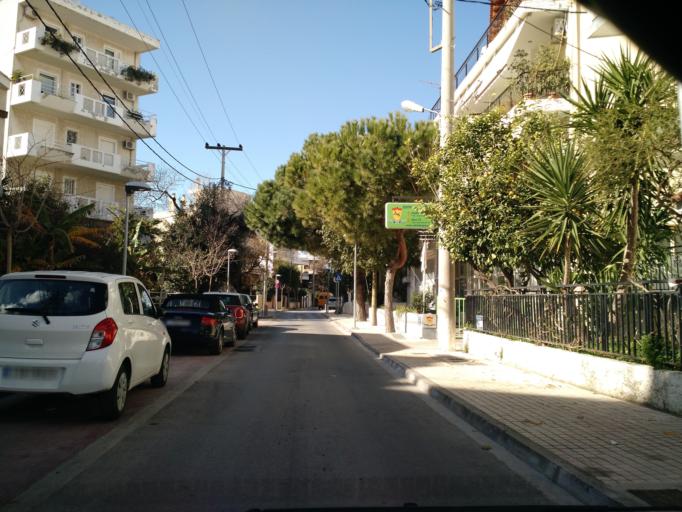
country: GR
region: Attica
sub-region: Nomarchia Athinas
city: Agia Paraskevi
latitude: 38.0199
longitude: 23.8229
